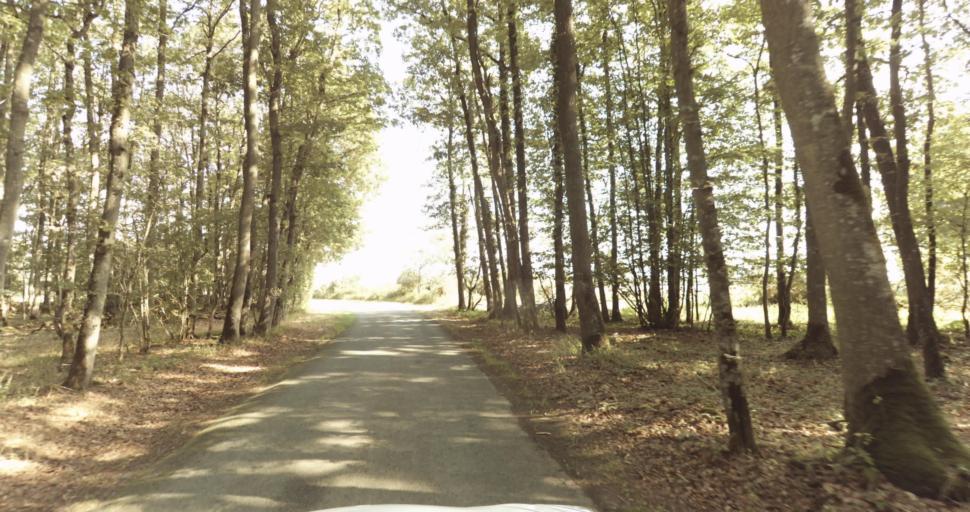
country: FR
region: Haute-Normandie
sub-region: Departement de l'Eure
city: Tillieres-sur-Avre
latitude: 48.7512
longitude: 1.1013
